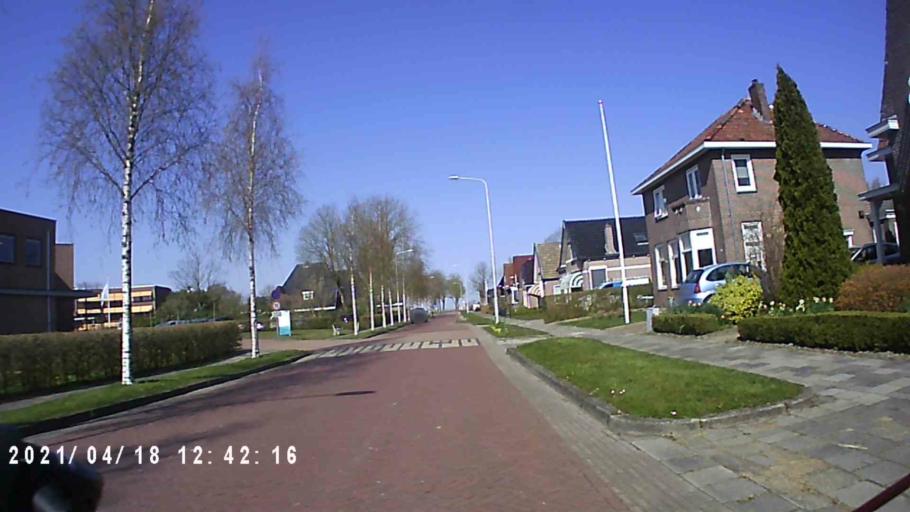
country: NL
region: Friesland
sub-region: Gemeente Dongeradeel
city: Anjum
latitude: 53.3615
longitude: 6.0652
